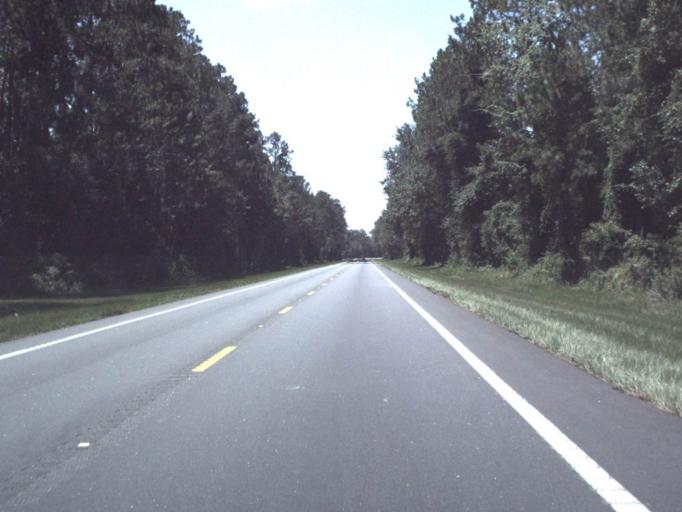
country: US
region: Florida
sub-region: Union County
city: Lake Butler
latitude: 30.0852
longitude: -82.2161
